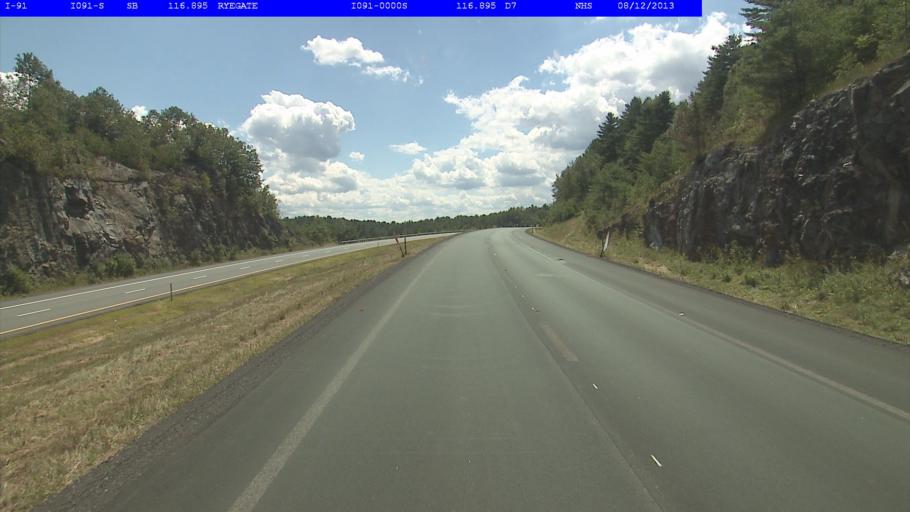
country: US
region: New Hampshire
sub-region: Grafton County
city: Woodsville
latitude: 44.2513
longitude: -72.0615
